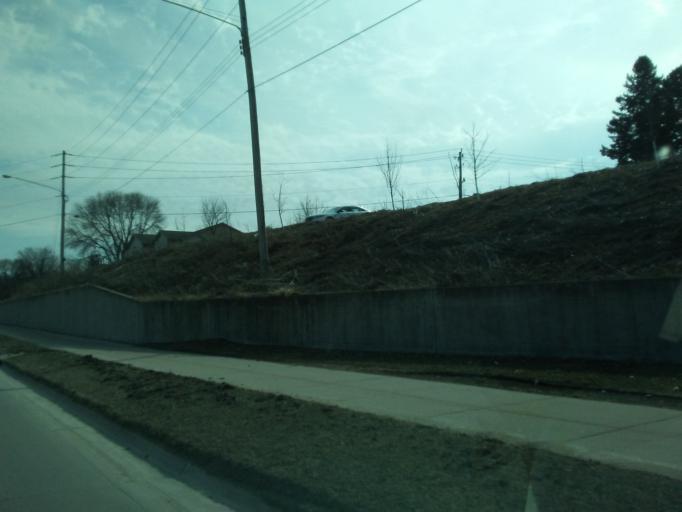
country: US
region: Iowa
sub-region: Winneshiek County
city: Decorah
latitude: 43.2974
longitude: -91.7733
